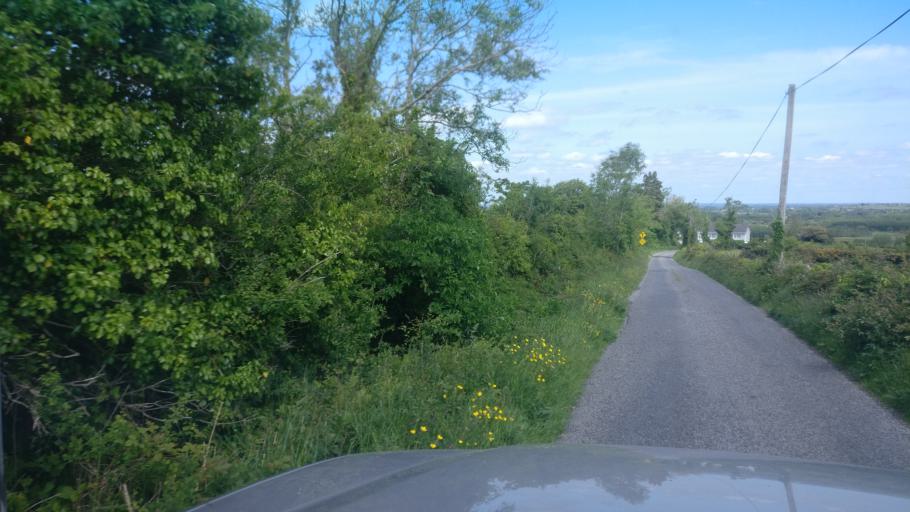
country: IE
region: Connaught
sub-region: County Galway
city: Loughrea
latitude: 53.1587
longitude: -8.6378
